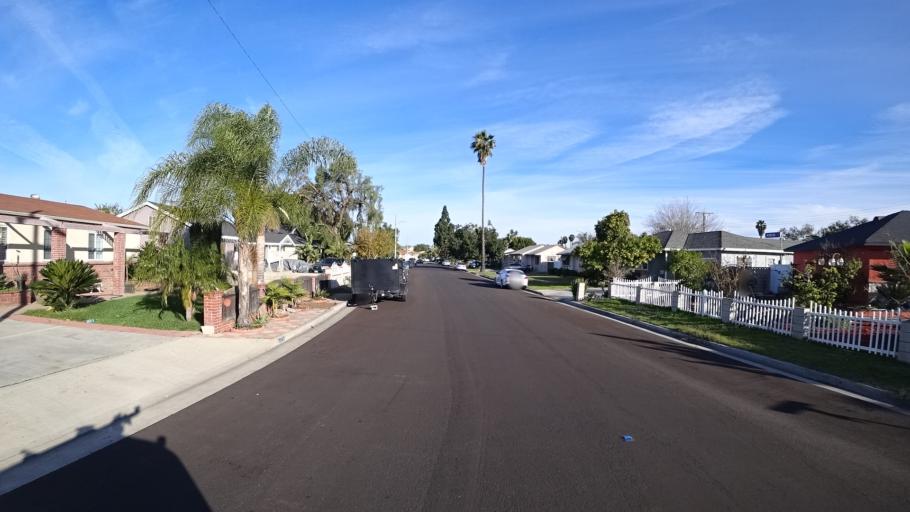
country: US
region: California
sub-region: Orange County
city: Garden Grove
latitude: 33.7678
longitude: -117.9399
